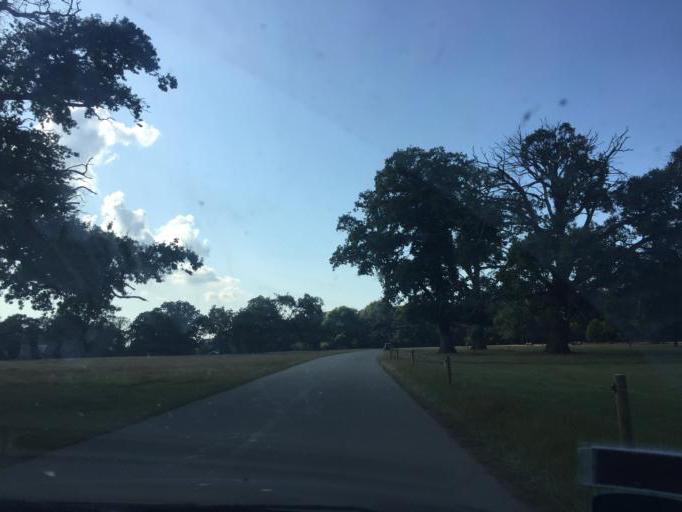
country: DK
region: Zealand
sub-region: Lolland Kommune
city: Maribo
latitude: 54.8254
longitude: 11.5054
